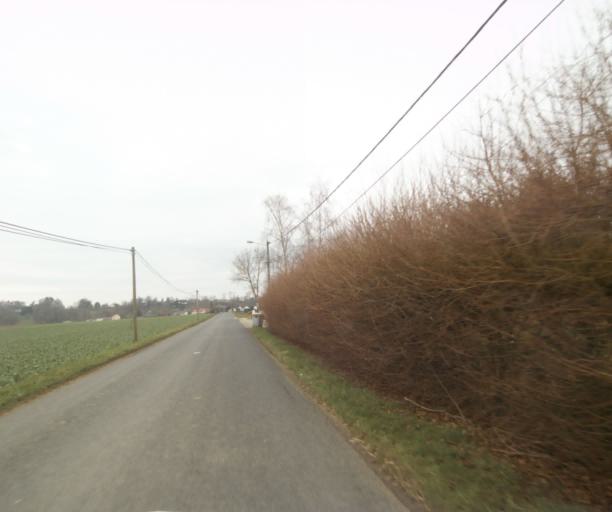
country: FR
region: Champagne-Ardenne
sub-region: Departement de la Haute-Marne
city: Villiers-en-Lieu
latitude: 48.6361
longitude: 4.8639
